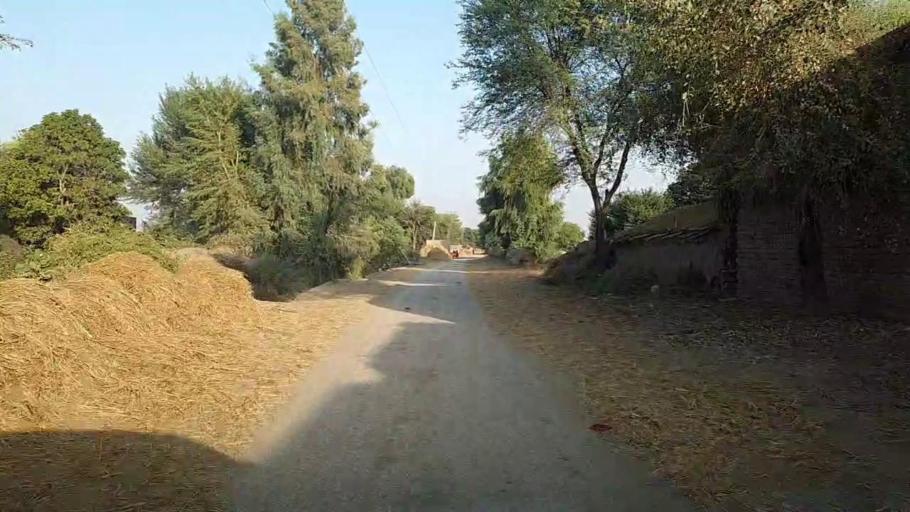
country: PK
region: Sindh
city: Kashmor
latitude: 28.4284
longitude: 69.4649
